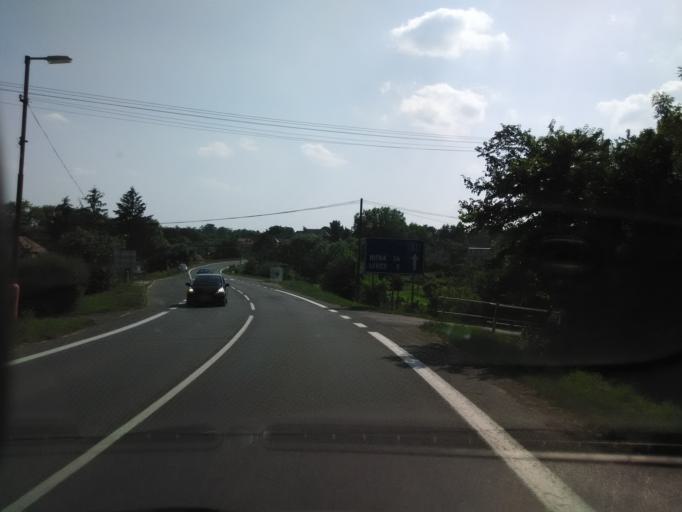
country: SK
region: Nitriansky
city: Levice
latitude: 48.2633
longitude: 18.7089
